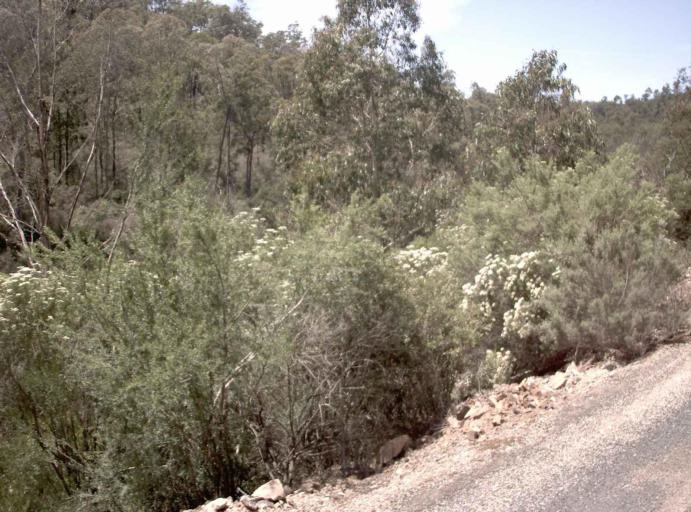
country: AU
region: Victoria
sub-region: East Gippsland
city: Lakes Entrance
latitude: -37.5536
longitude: 147.8780
